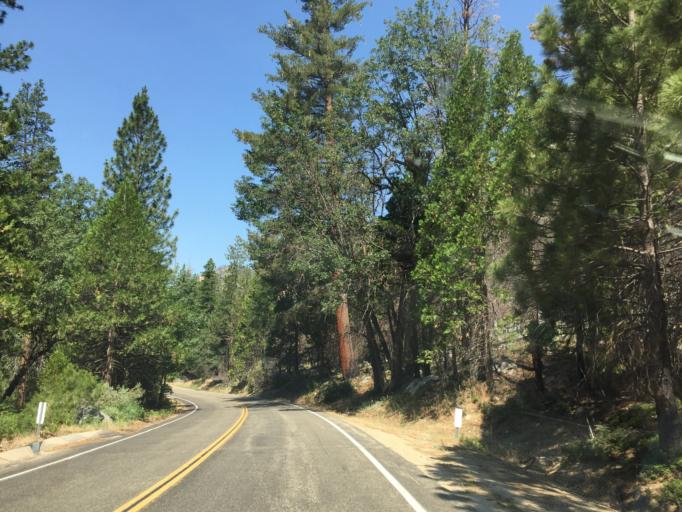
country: US
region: California
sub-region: Tulare County
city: Three Rivers
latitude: 36.8024
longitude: -118.6981
